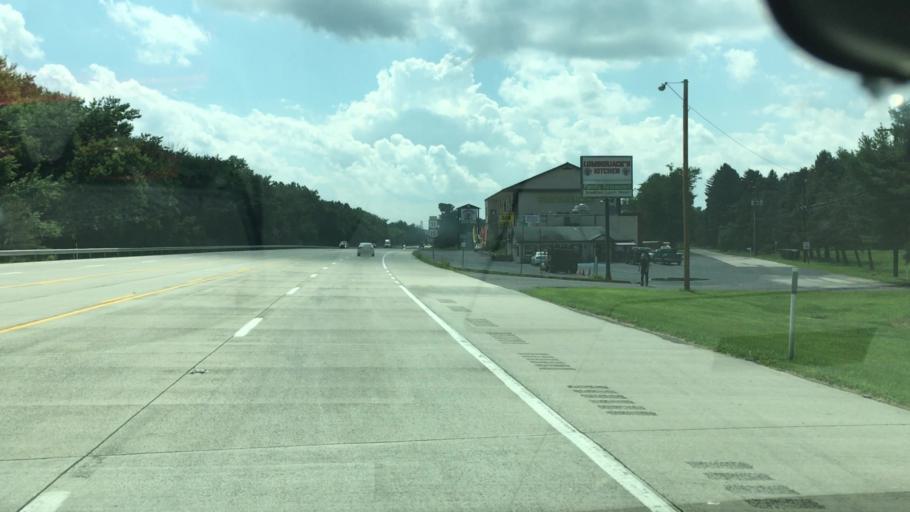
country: US
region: Pennsylvania
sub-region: Dauphin County
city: Matamoras
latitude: 40.4563
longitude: -76.9633
